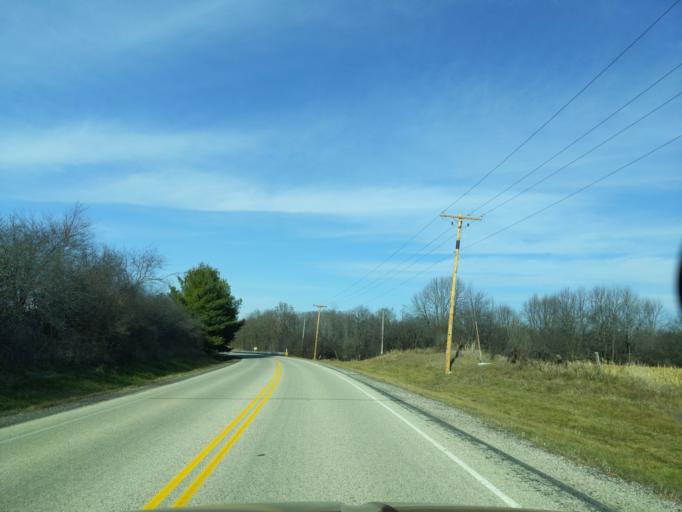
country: US
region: Wisconsin
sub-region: Walworth County
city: Elkhorn
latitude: 42.7480
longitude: -88.5925
